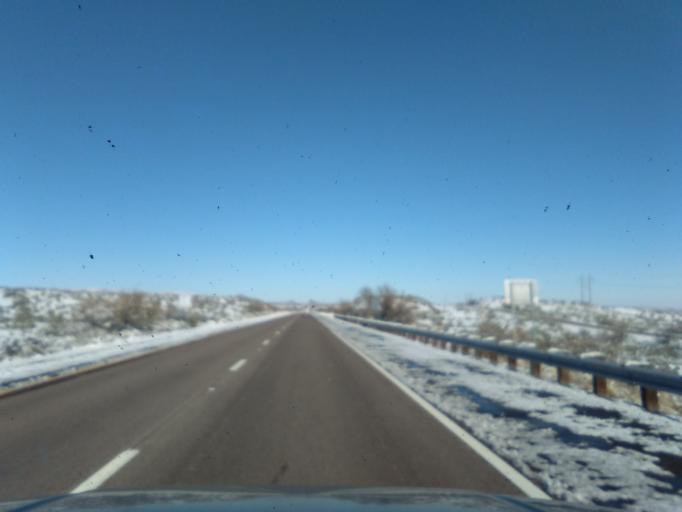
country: US
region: New Mexico
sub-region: Socorro County
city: Socorro
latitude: 33.6881
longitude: -107.0628
